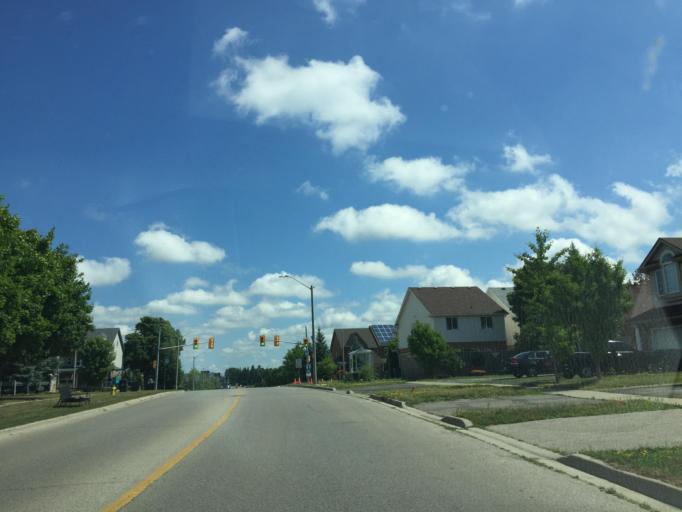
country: CA
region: Ontario
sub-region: Wellington County
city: Guelph
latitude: 43.5112
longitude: -80.2099
